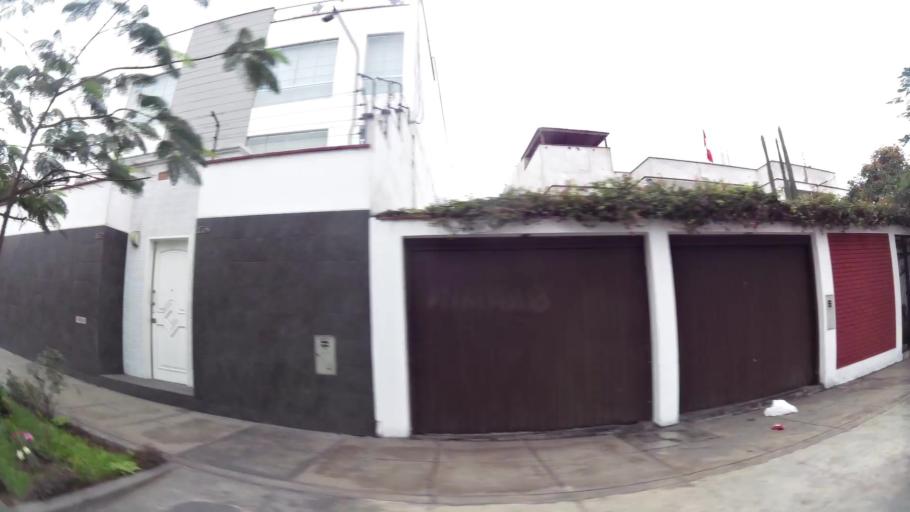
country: PE
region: Lima
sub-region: Lima
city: San Luis
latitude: -12.1014
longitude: -77.0088
